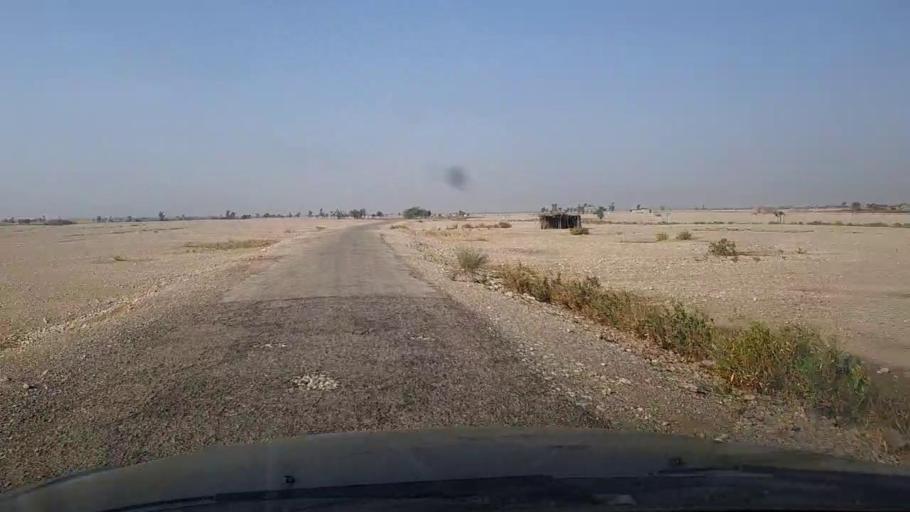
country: PK
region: Sindh
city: Sann
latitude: 26.0029
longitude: 68.0805
